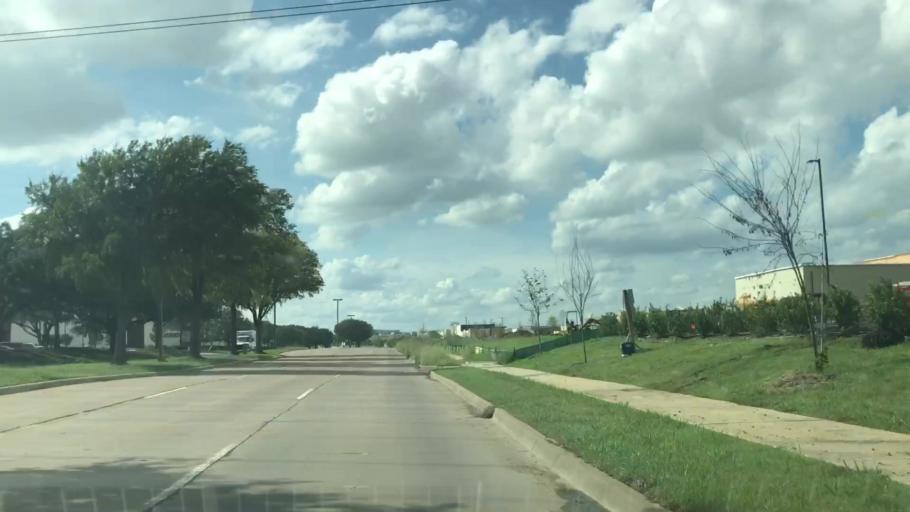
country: US
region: Texas
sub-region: Dallas County
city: Coppell
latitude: 32.9194
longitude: -96.9844
